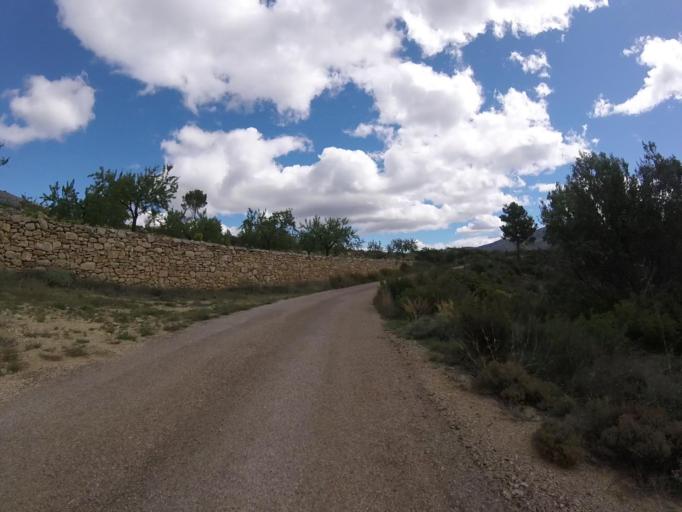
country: ES
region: Valencia
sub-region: Provincia de Castello
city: Sierra-Engarceran
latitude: 40.2829
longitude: -0.0714
